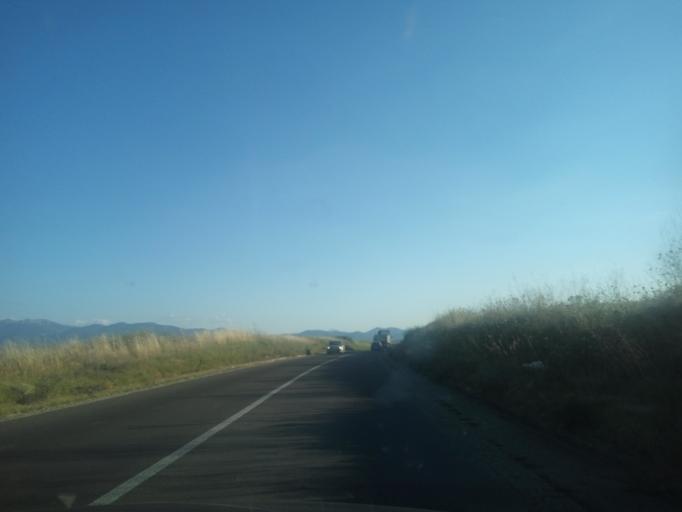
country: XK
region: Gjakova
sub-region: Komuna e Gjakoves
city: Gjakove
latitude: 42.4428
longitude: 20.4908
